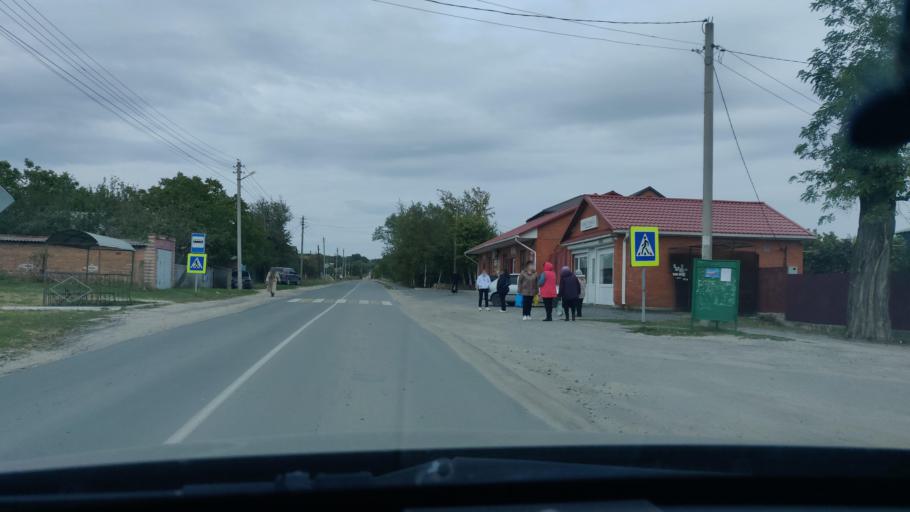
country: RU
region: Rostov
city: Ust'-Donetskiy
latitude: 47.6603
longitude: 40.9196
